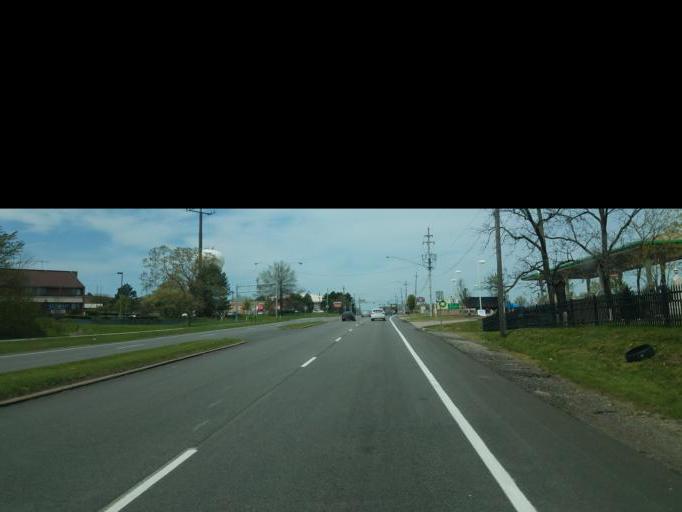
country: US
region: Ohio
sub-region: Lake County
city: Wickliffe
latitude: 41.6034
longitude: -81.4399
